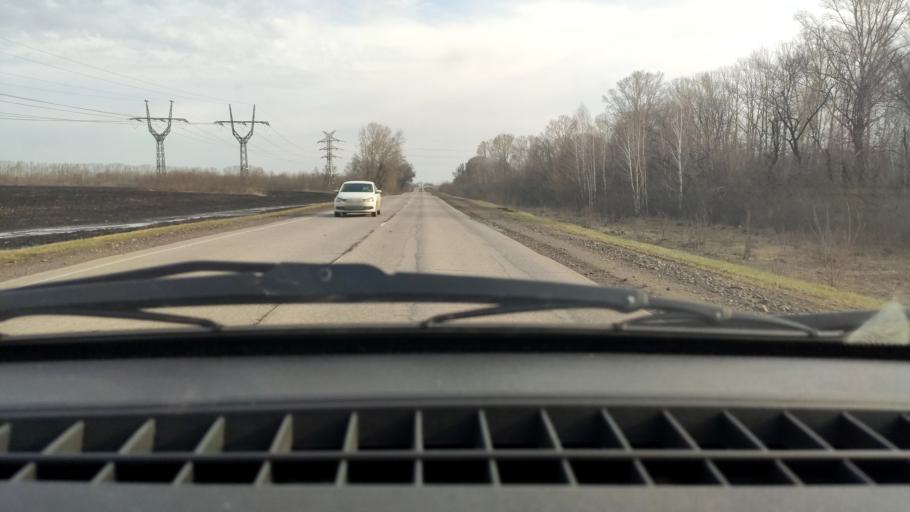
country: RU
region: Bashkortostan
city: Chishmy
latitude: 54.5181
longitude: 55.2964
